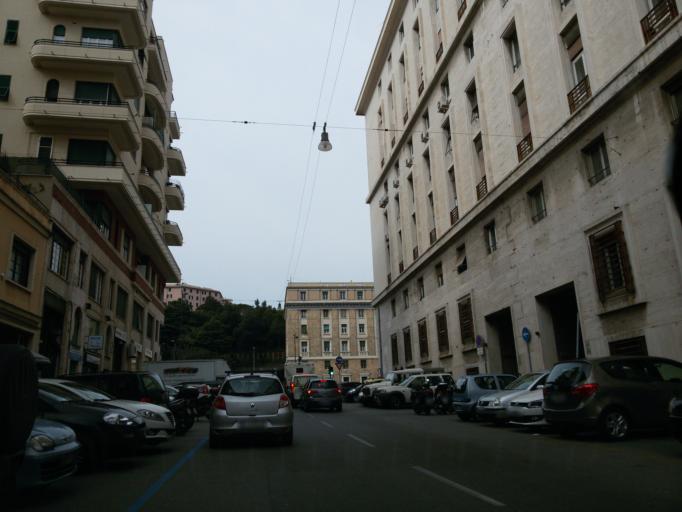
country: IT
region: Liguria
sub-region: Provincia di Genova
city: San Teodoro
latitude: 44.4000
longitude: 8.9464
